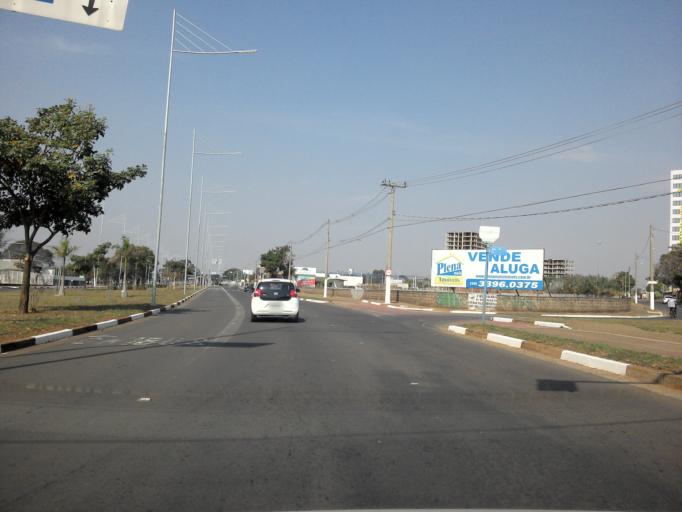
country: BR
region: Sao Paulo
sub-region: Hortolandia
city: Hortolandia
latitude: -22.8734
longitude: -47.2107
